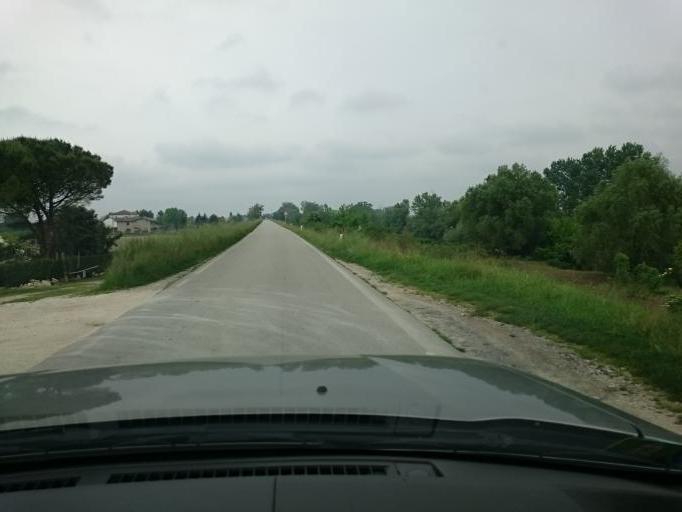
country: IT
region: Veneto
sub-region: Provincia di Padova
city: Campagnola
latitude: 45.2591
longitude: 11.9814
